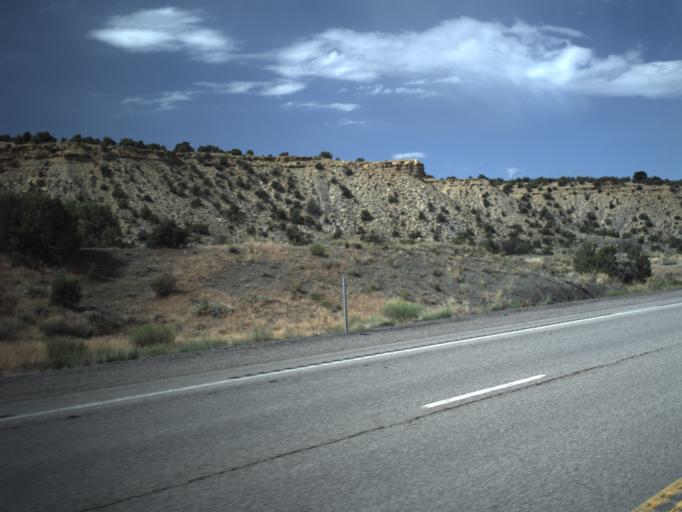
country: US
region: Utah
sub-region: Carbon County
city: Wellington
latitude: 39.5469
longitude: -110.6437
